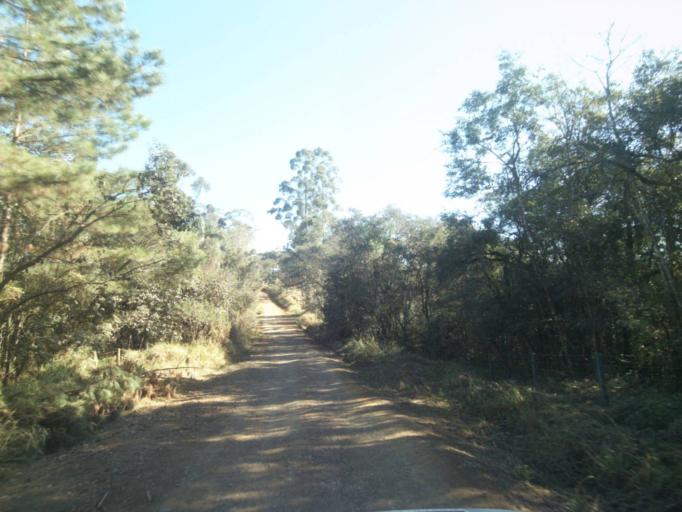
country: BR
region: Parana
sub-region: Tibagi
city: Tibagi
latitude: -24.5407
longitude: -50.5026
